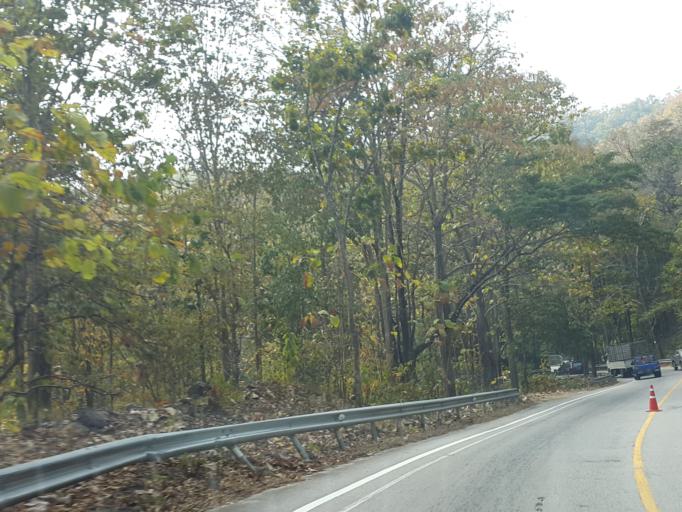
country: TH
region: Chiang Mai
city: Hot
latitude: 18.1996
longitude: 98.4509
